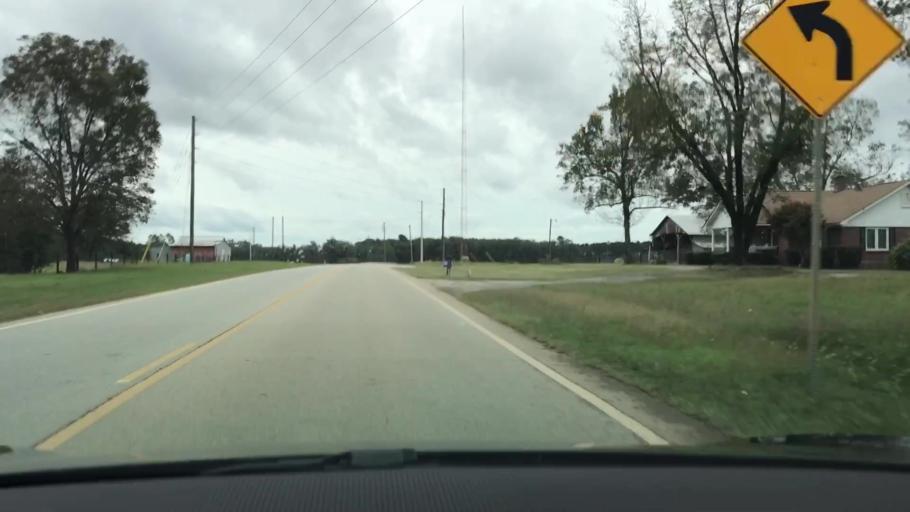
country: US
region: Georgia
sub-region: Jefferson County
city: Wrens
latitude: 33.1632
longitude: -82.4562
